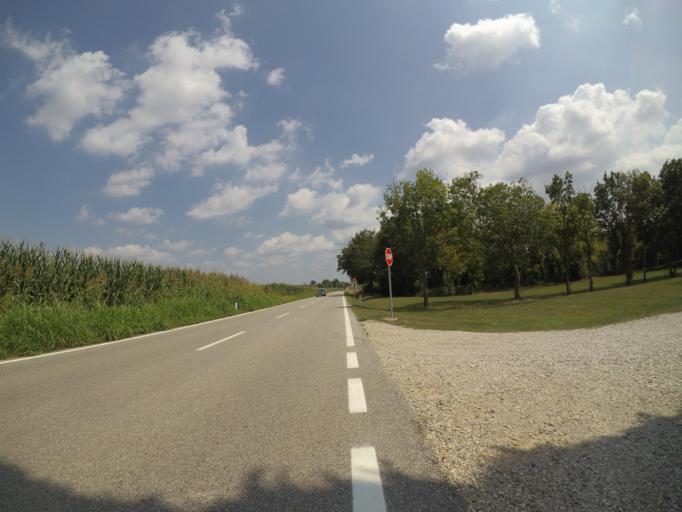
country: IT
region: Friuli Venezia Giulia
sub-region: Provincia di Udine
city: Mereto di Tomba
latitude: 46.0191
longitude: 13.0250
